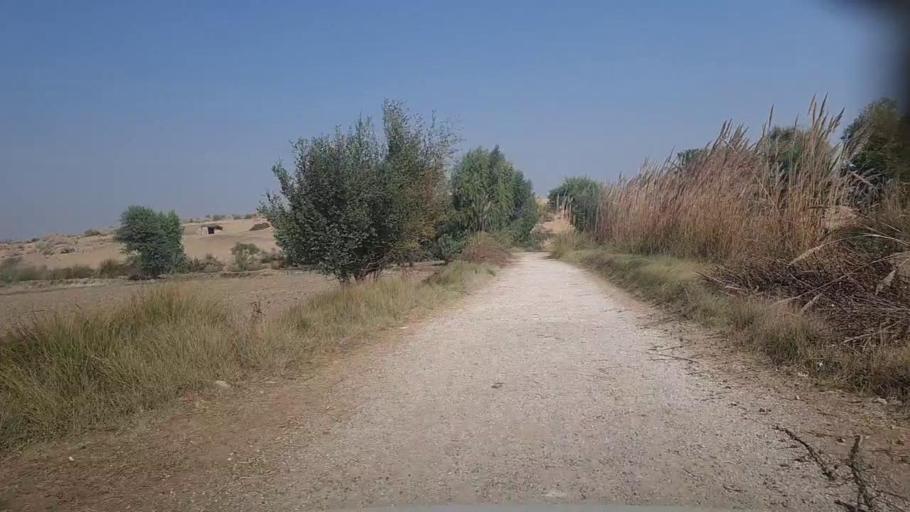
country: PK
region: Sindh
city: Kandiari
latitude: 26.9419
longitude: 68.5325
